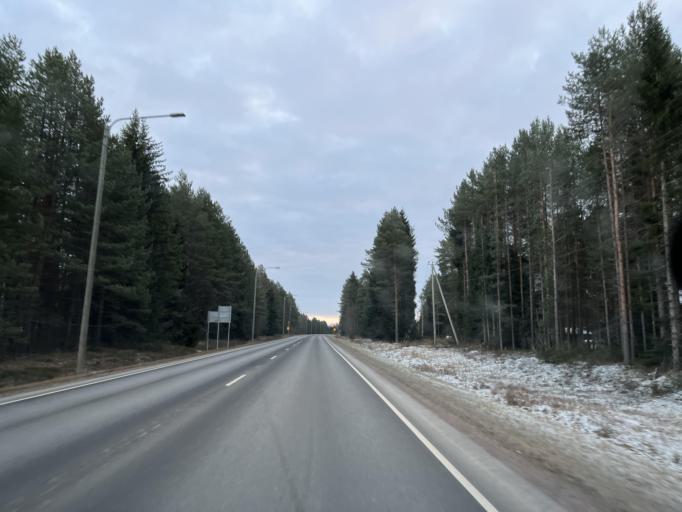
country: FI
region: Northern Ostrobothnia
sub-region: Oulu
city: Muhos
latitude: 64.8675
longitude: 25.8738
